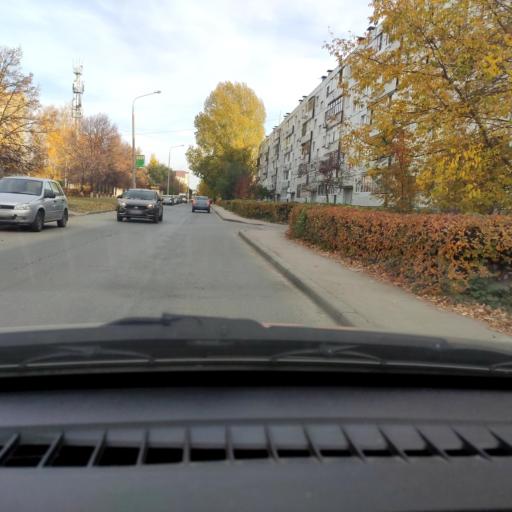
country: RU
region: Samara
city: Tol'yatti
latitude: 53.5248
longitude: 49.3084
